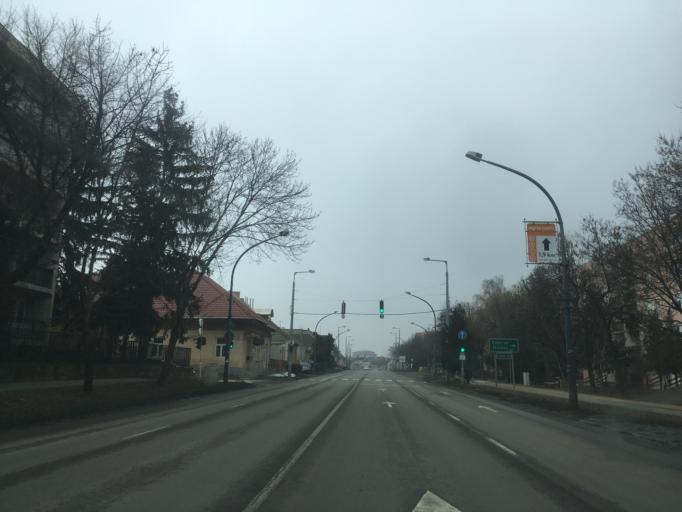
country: HU
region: Heves
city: Eger
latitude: 47.8871
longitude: 20.3807
